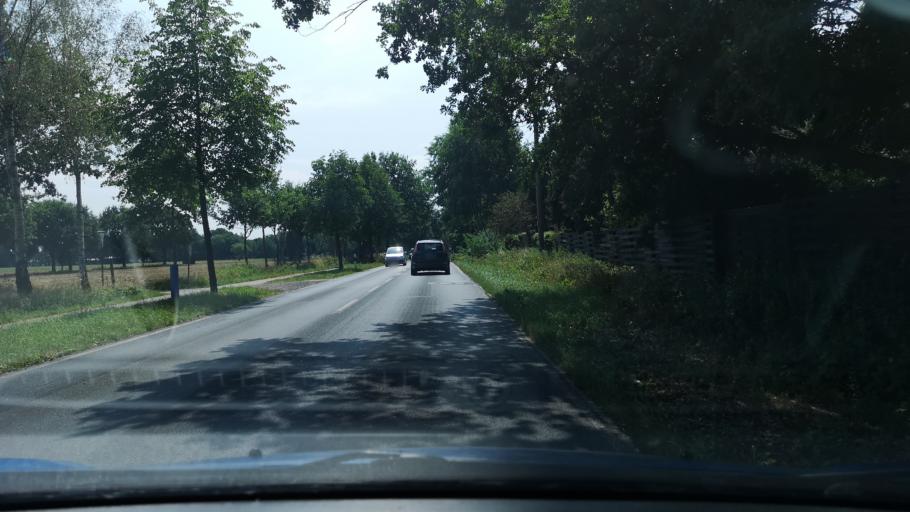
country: DE
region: Lower Saxony
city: Isernhagen Farster Bauerschaft
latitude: 52.4427
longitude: 9.8005
